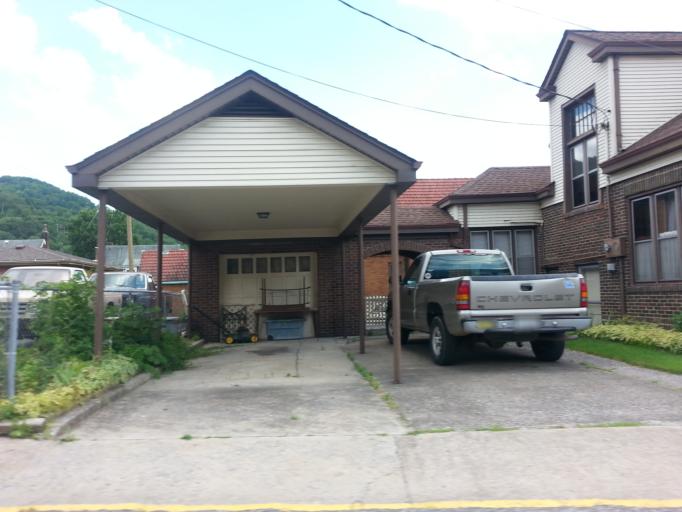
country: US
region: Kentucky
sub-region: Harlan County
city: Harlan
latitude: 36.8481
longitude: -83.3213
